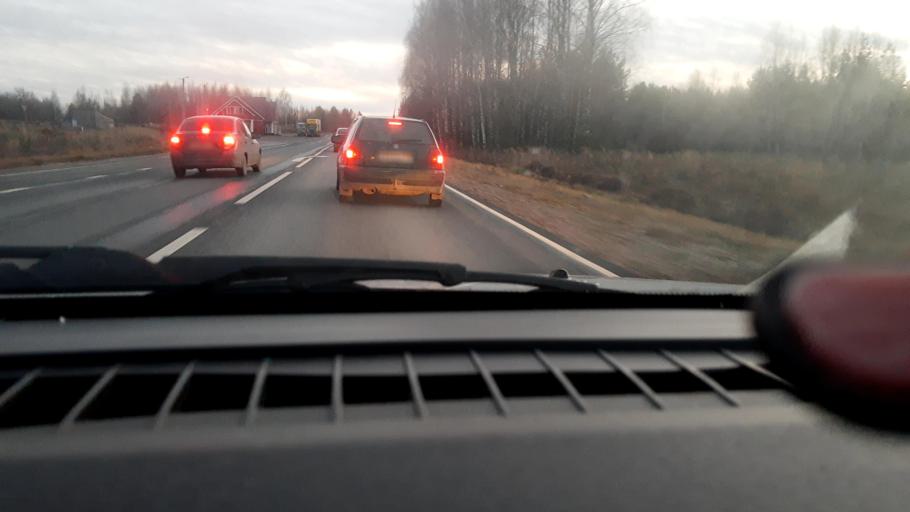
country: RU
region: Nizjnij Novgorod
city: Krasnyye Baki
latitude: 57.0179
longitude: 45.1167
